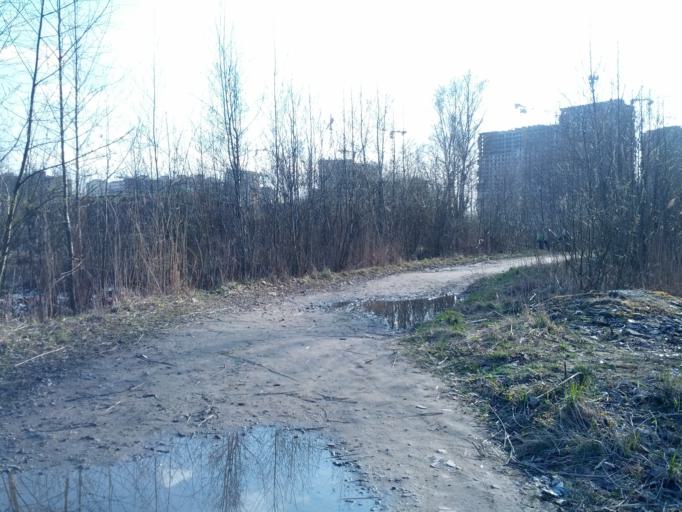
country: RU
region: Leningrad
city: Rybatskoye
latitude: 59.9120
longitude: 30.5227
